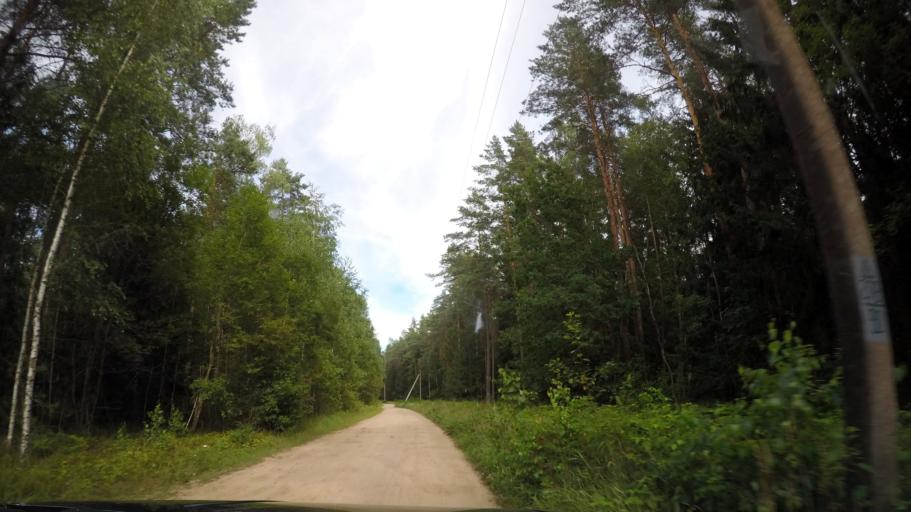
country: BY
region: Grodnenskaya
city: Skidal'
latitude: 53.8413
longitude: 24.2029
